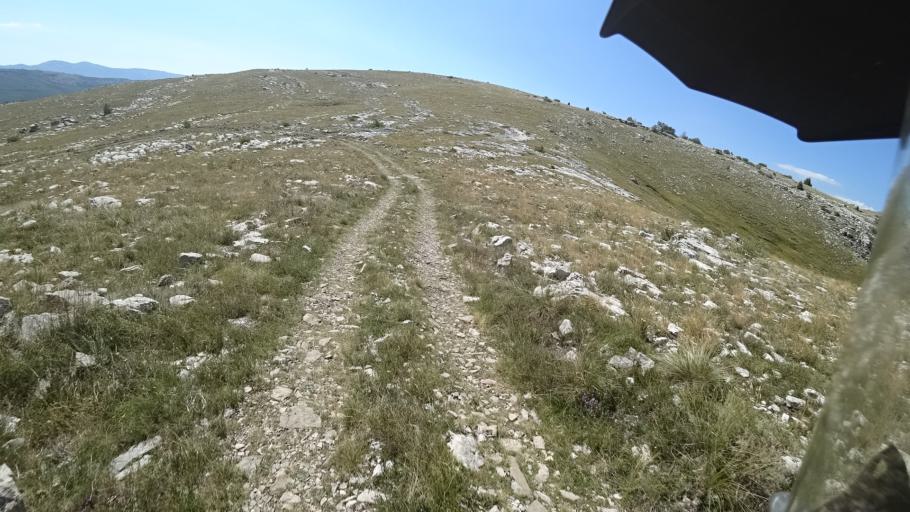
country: HR
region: Splitsko-Dalmatinska
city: Hrvace
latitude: 43.9008
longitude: 16.5903
